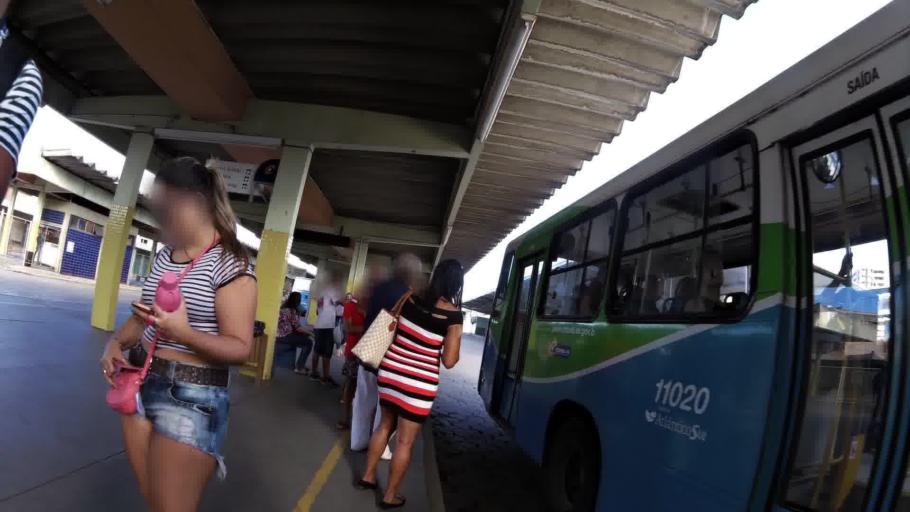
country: BR
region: Espirito Santo
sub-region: Vila Velha
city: Vila Velha
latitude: -20.3425
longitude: -40.2951
